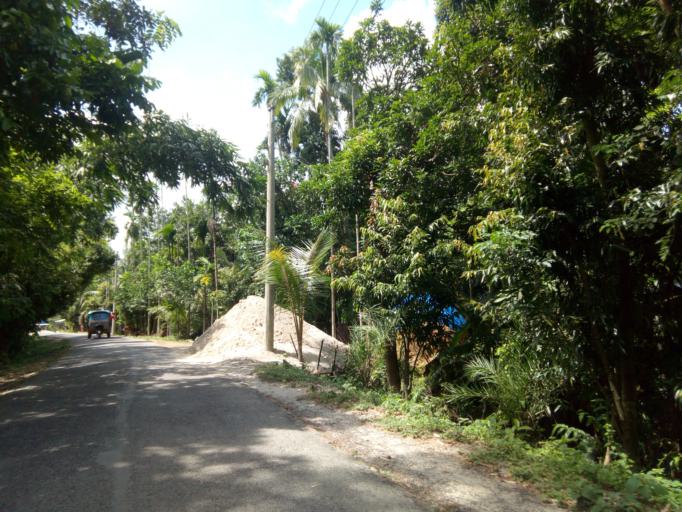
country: BD
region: Khulna
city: Kalia
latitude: 23.0168
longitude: 89.7178
